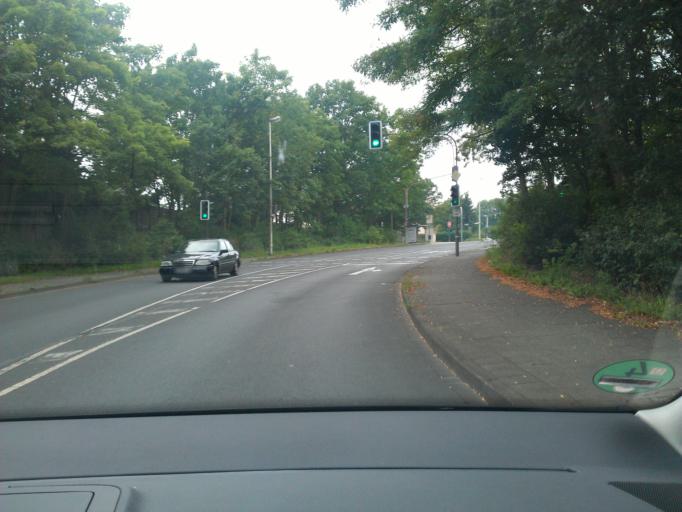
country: DE
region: North Rhine-Westphalia
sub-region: Regierungsbezirk Dusseldorf
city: Hilden
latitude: 51.1637
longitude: 6.9486
